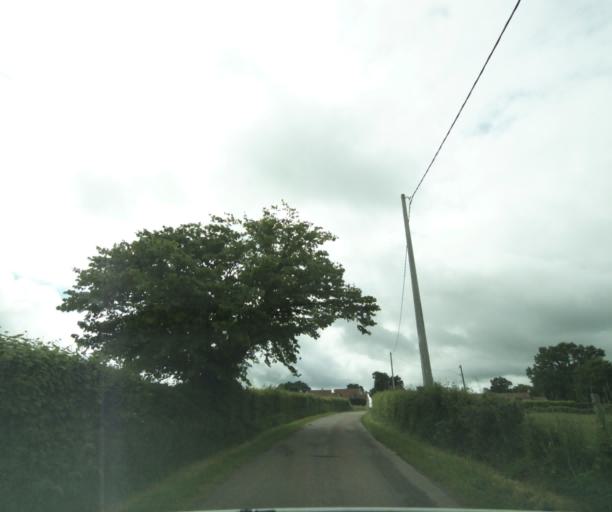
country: FR
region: Bourgogne
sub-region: Departement de Saone-et-Loire
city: Charolles
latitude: 46.4217
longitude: 4.3051
